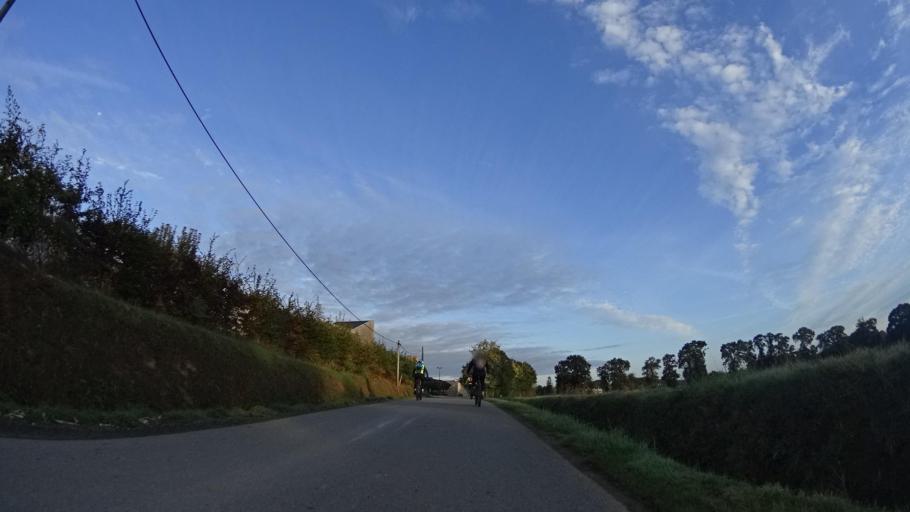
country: FR
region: Brittany
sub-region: Departement des Cotes-d'Armor
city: Evran
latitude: 48.3621
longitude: -1.9520
